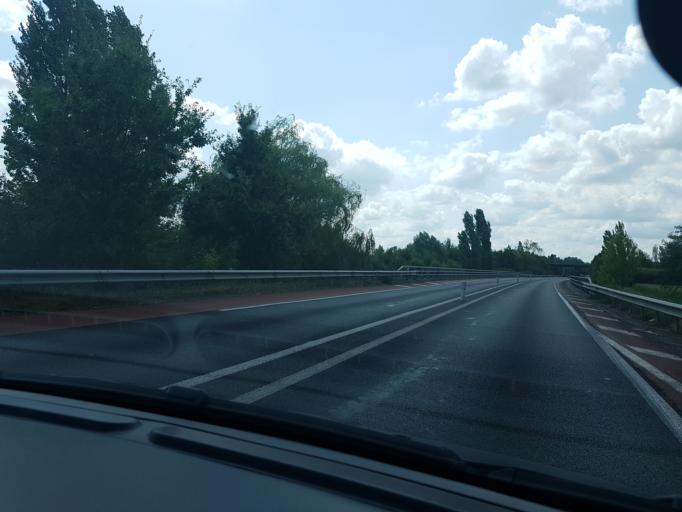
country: FR
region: Aquitaine
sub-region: Departement de la Gironde
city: Genissac
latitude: 44.8721
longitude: -0.2341
